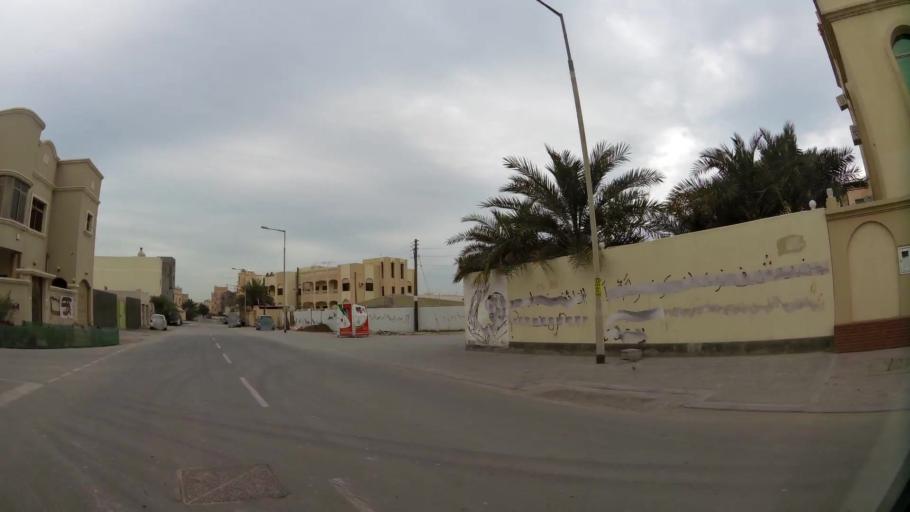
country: BH
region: Northern
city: Sitrah
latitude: 26.1700
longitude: 50.6079
